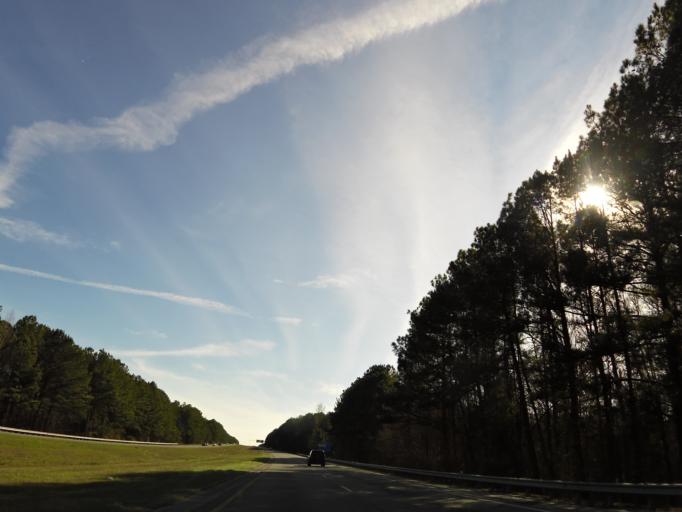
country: US
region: Alabama
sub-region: Russell County
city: Phenix City
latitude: 32.5801
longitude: -84.9615
